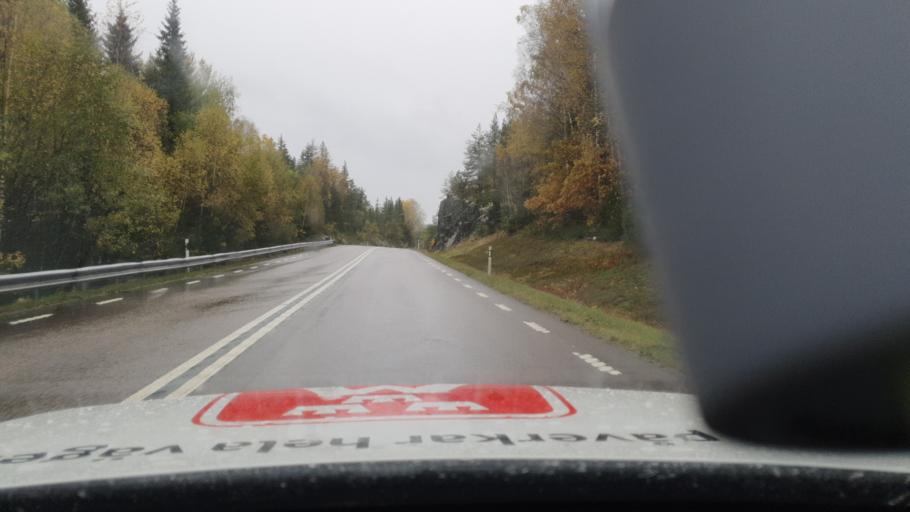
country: SE
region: Vaestra Goetaland
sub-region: Dals-Ed Kommun
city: Ed
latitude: 58.9329
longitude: 12.0439
